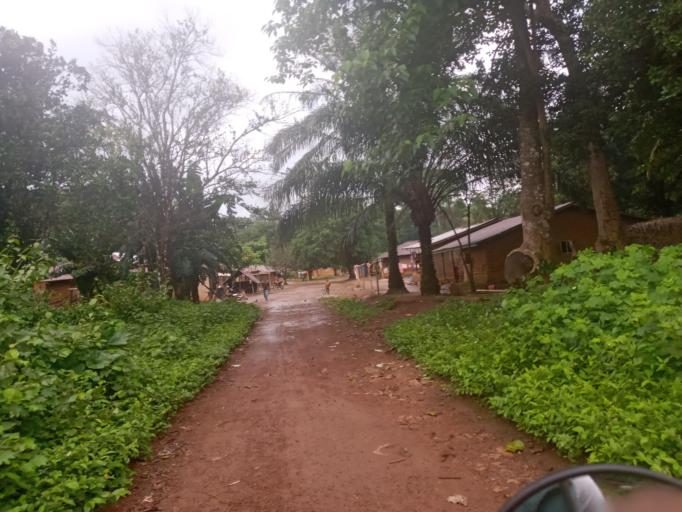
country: SL
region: Northern Province
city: Bumbuna
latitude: 8.9442
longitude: -11.7504
